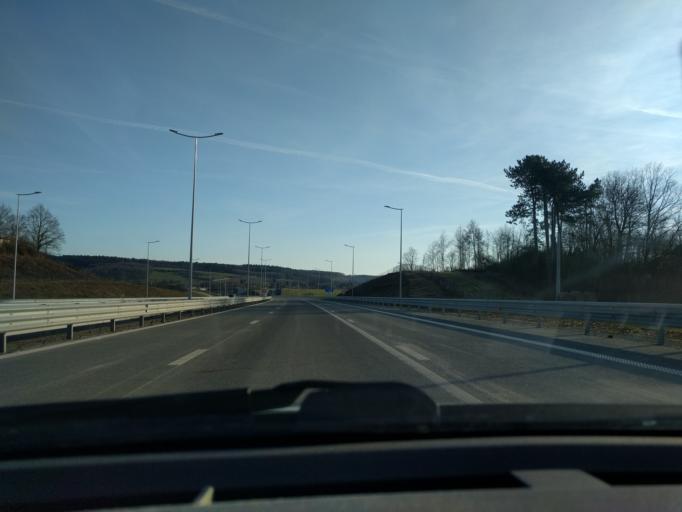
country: BE
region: Wallonia
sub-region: Province de Namur
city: Couvin
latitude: 50.0591
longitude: 4.5058
